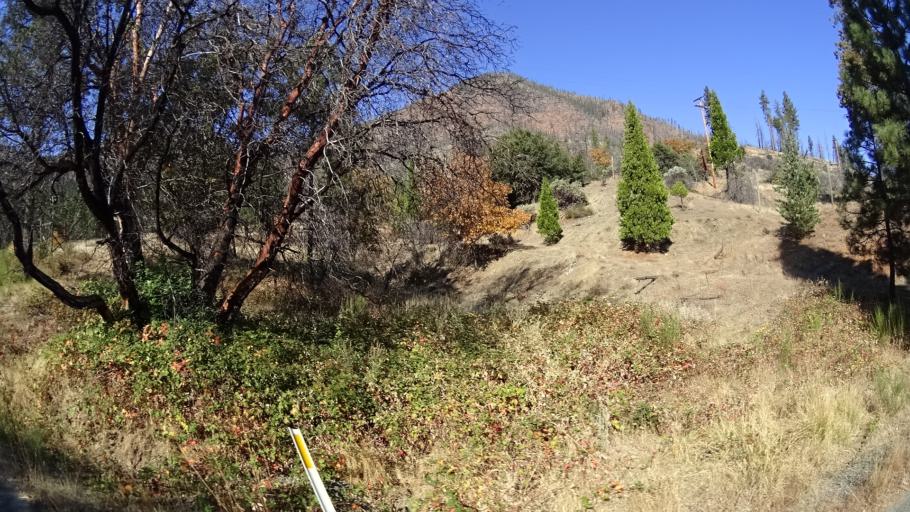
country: US
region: California
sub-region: Siskiyou County
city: Happy Camp
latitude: 41.7154
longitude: -123.0231
